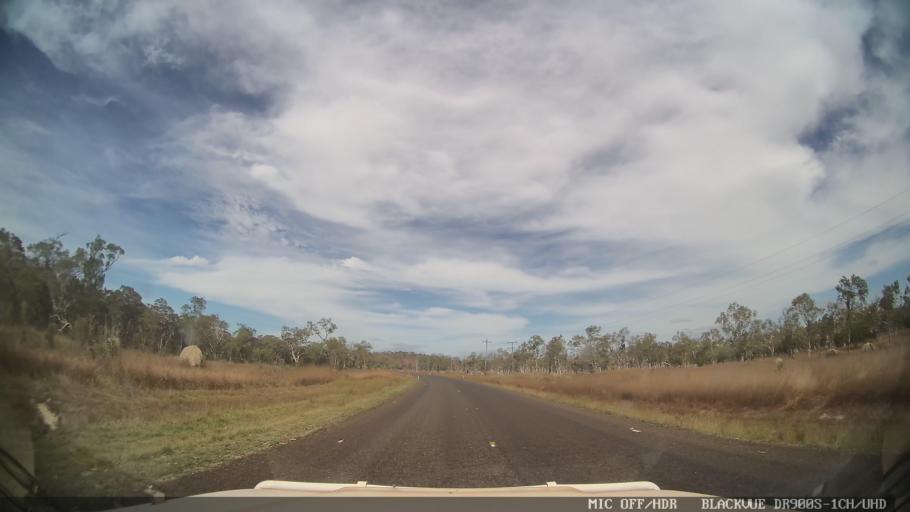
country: AU
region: Queensland
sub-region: Tablelands
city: Mareeba
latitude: -16.8507
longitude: 145.3836
